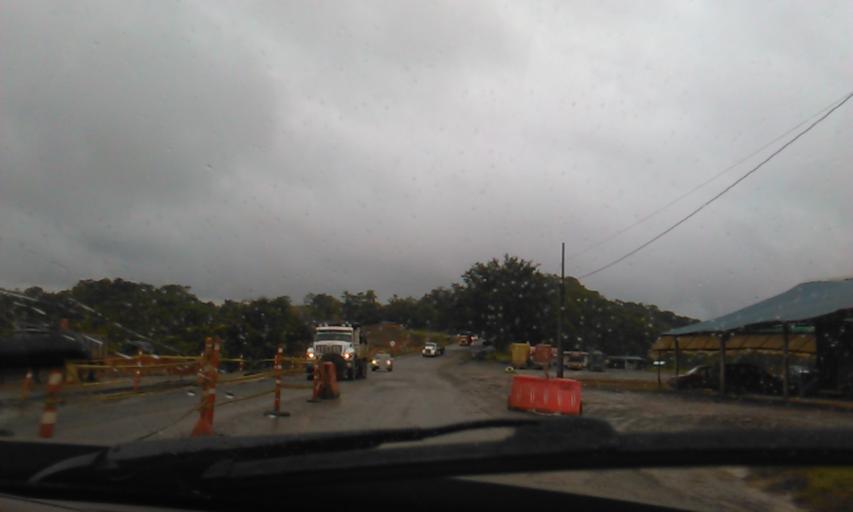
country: CO
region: Valle del Cauca
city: Buenaventura
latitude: 3.8778
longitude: -76.8906
